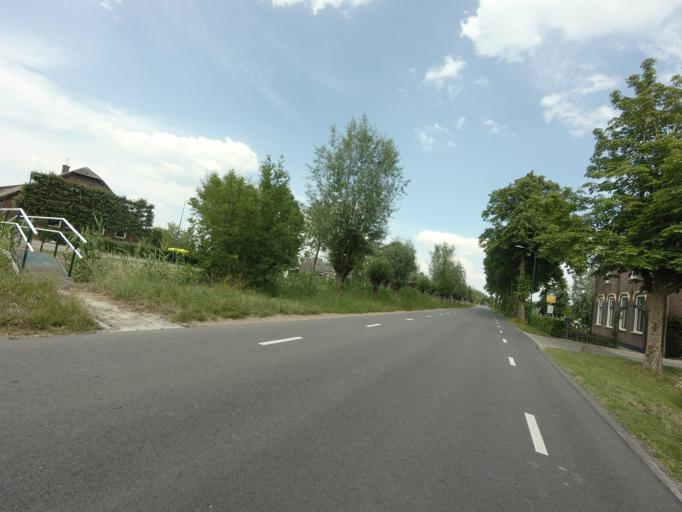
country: NL
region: Utrecht
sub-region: Gemeente Oudewater
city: Oudewater
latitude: 51.9904
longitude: 4.8892
